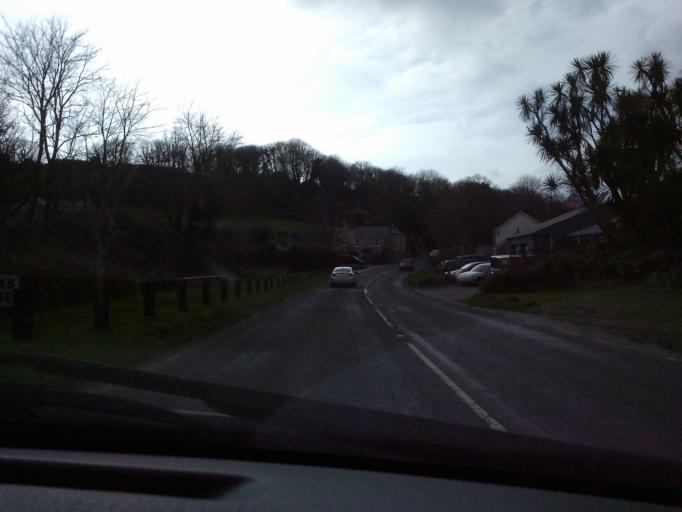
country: GB
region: England
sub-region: Cornwall
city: Penzance
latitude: 50.1071
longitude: -5.5709
